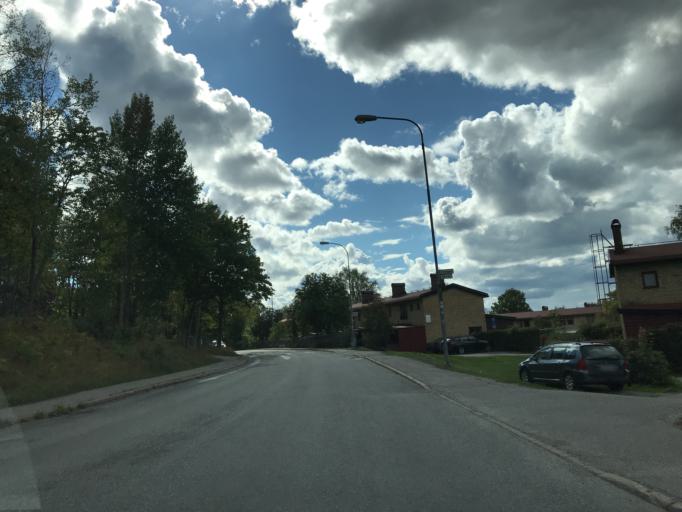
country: SE
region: Stockholm
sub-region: Sollentuna Kommun
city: Sollentuna
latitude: 59.4430
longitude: 17.9648
